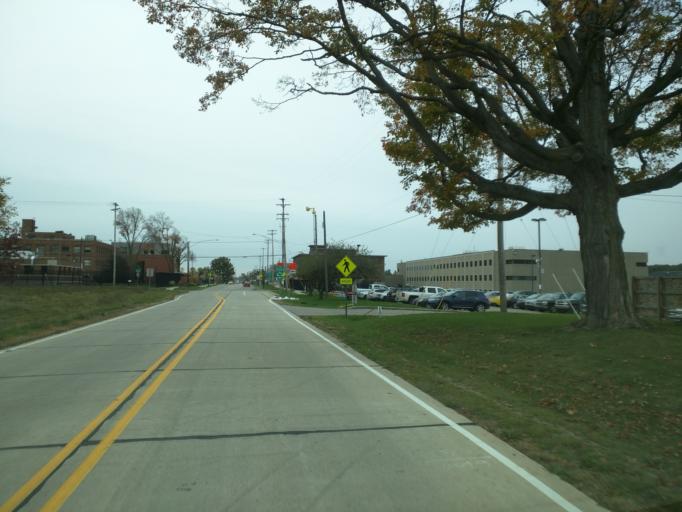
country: US
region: Michigan
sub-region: Ingham County
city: Edgemont Park
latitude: 42.7707
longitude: -84.5674
